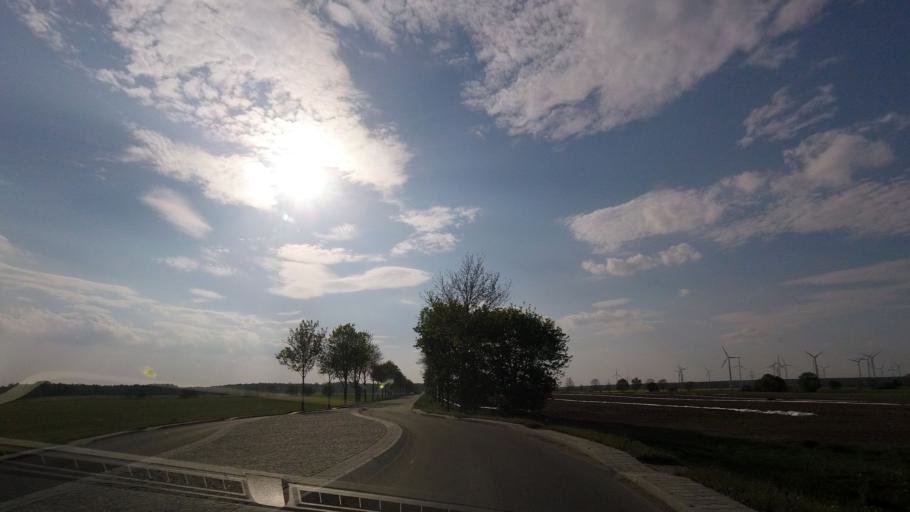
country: DE
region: Brandenburg
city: Drahnsdorf
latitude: 51.8508
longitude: 13.5236
